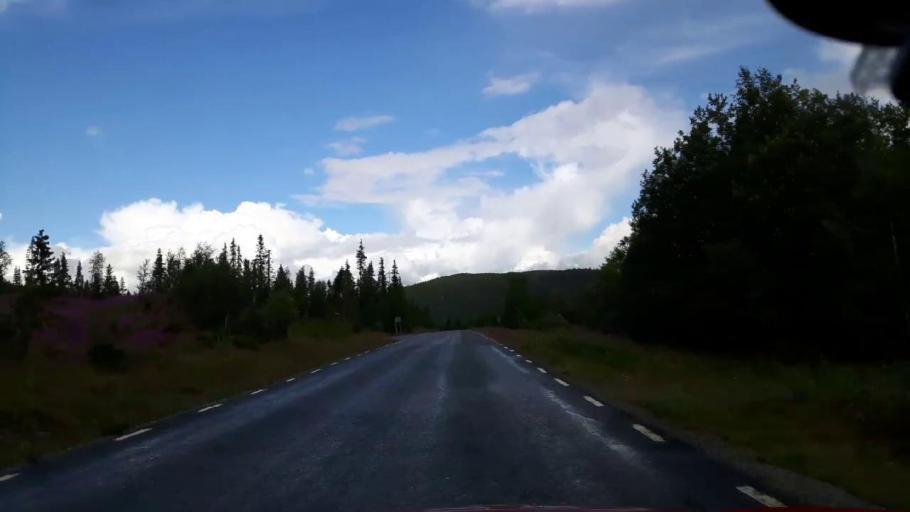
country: SE
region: Vaesterbotten
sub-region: Vilhelmina Kommun
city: Sjoberg
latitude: 65.0149
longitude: 15.1709
